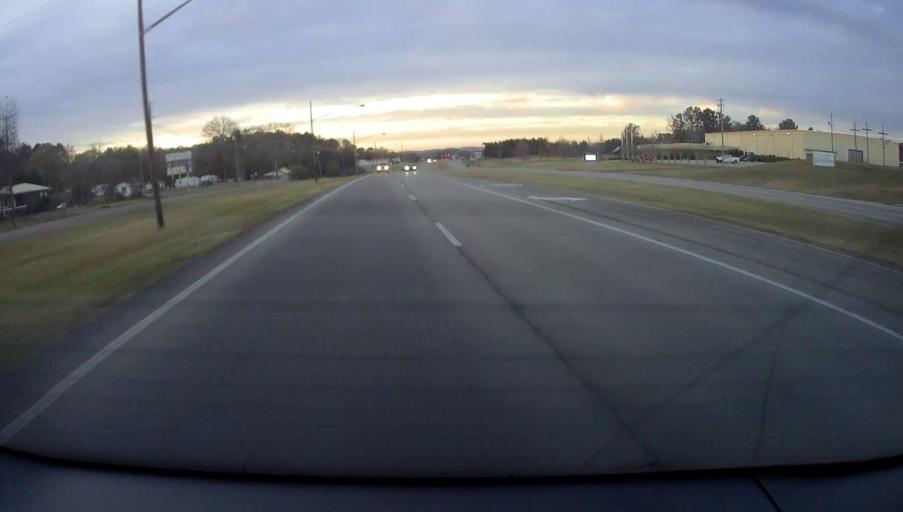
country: US
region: Alabama
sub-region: Etowah County
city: Glencoe
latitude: 33.9688
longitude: -85.9464
